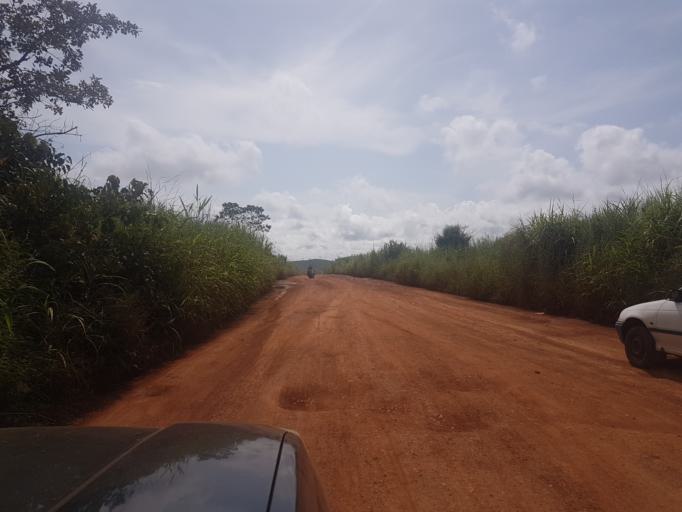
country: GN
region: Nzerekore
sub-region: Prefecture de Guekedou
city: Gueckedou
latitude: 8.6995
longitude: -10.1245
